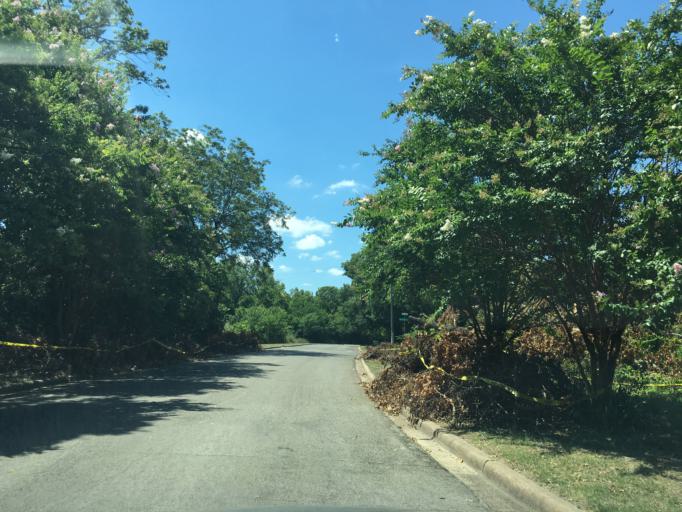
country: US
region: Texas
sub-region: Dallas County
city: Garland
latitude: 32.8482
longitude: -96.7018
